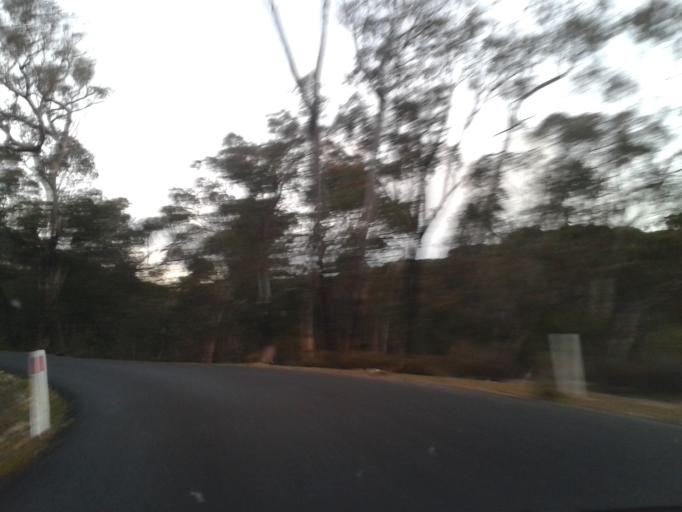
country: AU
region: Victoria
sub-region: Northern Grampians
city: Stawell
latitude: -37.1630
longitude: 142.4942
